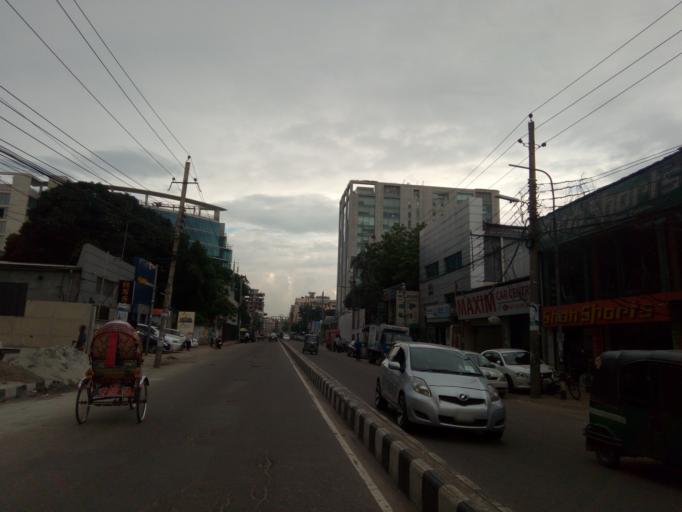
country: BD
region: Dhaka
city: Paltan
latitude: 23.7708
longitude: 90.4051
